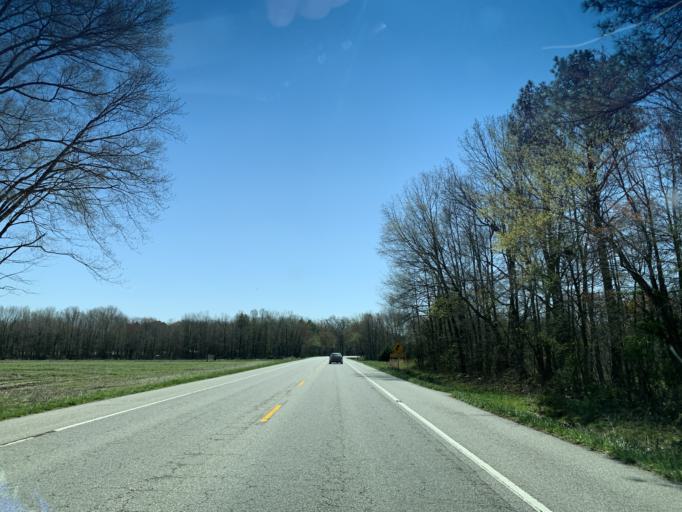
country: US
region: Maryland
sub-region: Queen Anne's County
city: Centreville
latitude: 38.9730
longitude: -76.0035
